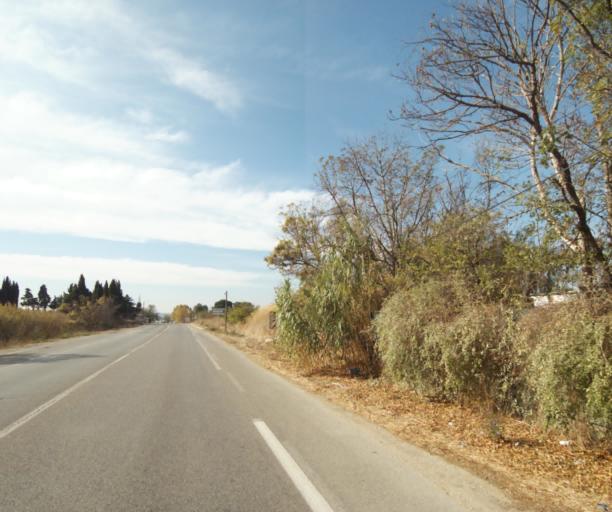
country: FR
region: Provence-Alpes-Cote d'Azur
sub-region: Departement des Bouches-du-Rhone
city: Le Rove
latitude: 43.4010
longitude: 5.2677
